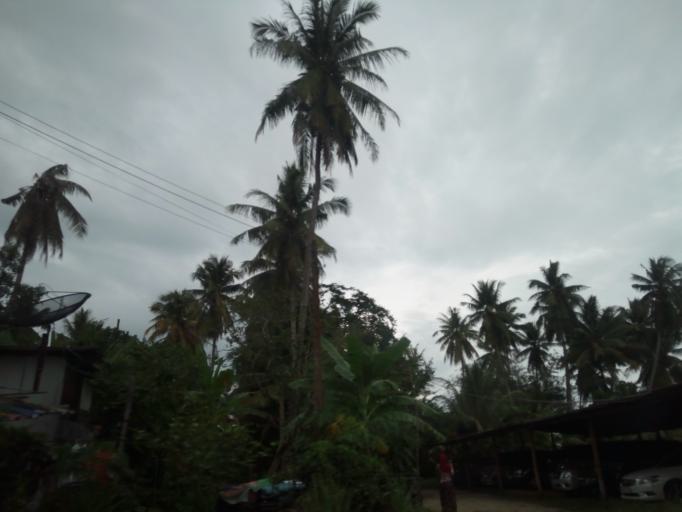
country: TH
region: Phuket
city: Thalang
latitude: 8.0505
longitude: 98.4115
